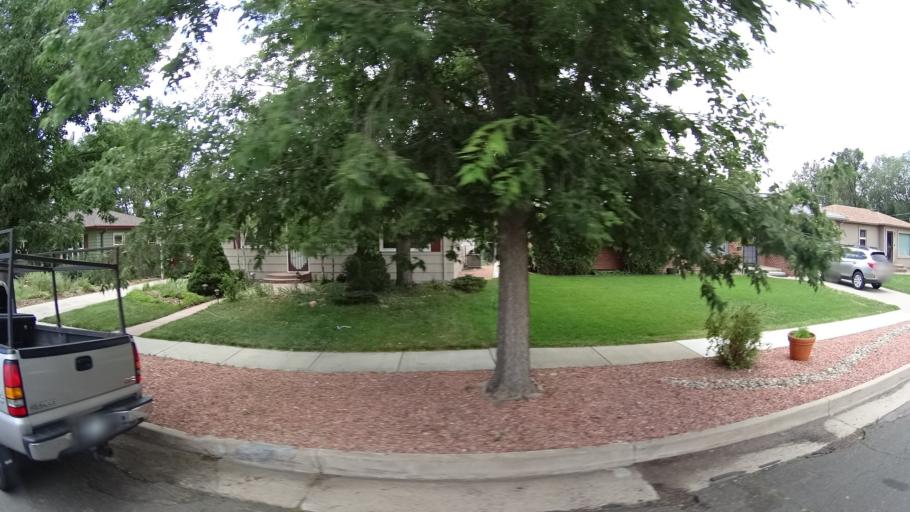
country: US
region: Colorado
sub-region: El Paso County
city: Colorado Springs
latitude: 38.8652
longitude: -104.8073
